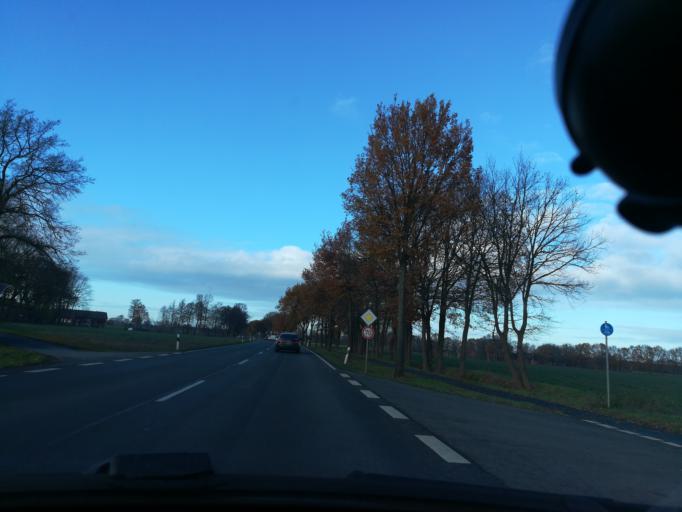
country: DE
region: Lower Saxony
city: Raddestorf
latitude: 52.4514
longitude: 8.9254
